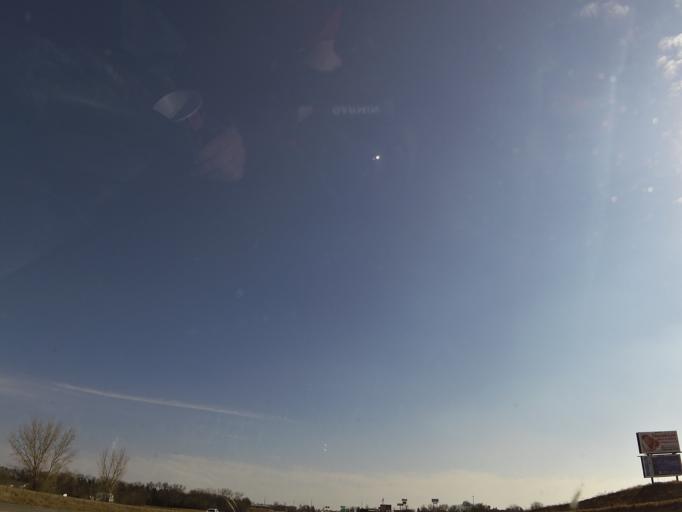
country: US
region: Minnesota
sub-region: Steele County
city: Owatonna
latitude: 44.1030
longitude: -93.2457
